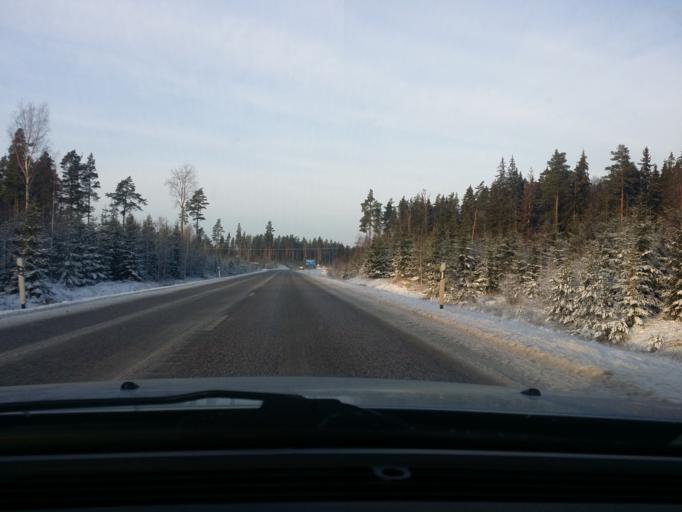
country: SE
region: OErebro
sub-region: Lindesbergs Kommun
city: Frovi
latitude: 59.4761
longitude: 15.3883
